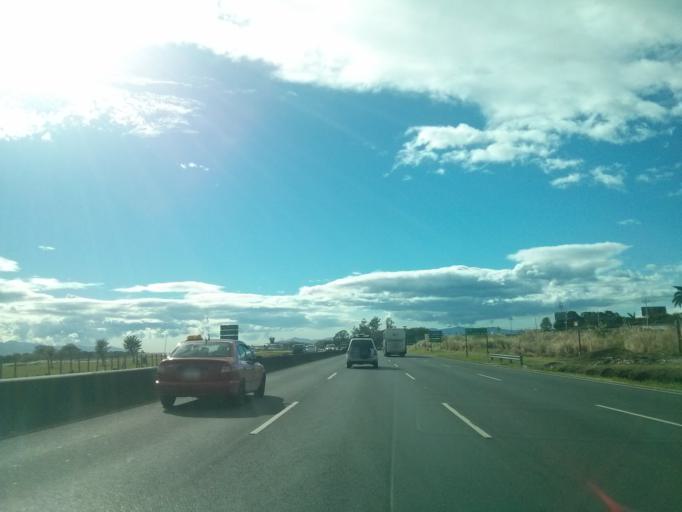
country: CR
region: Heredia
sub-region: Canton de Belen
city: San Antonio
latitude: 10.0002
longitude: -84.1913
